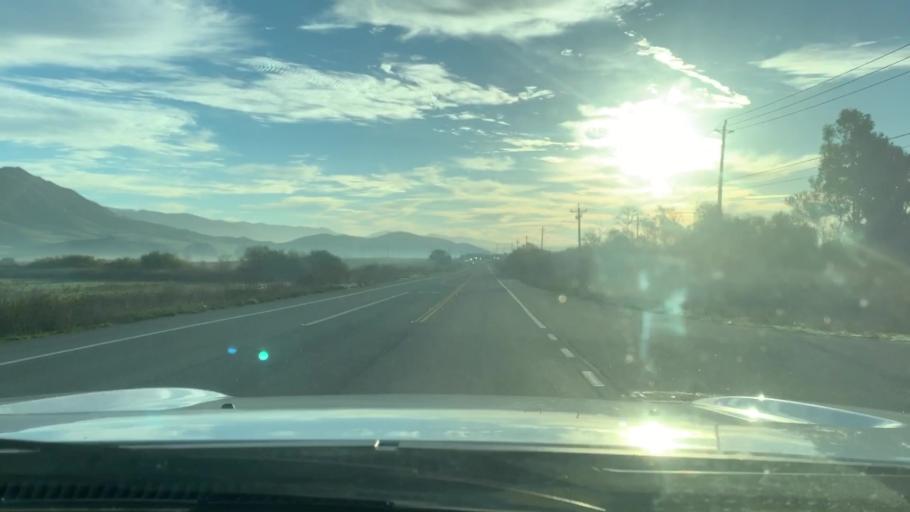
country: US
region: California
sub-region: San Luis Obispo County
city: San Luis Obispo
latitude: 35.2791
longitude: -120.7181
